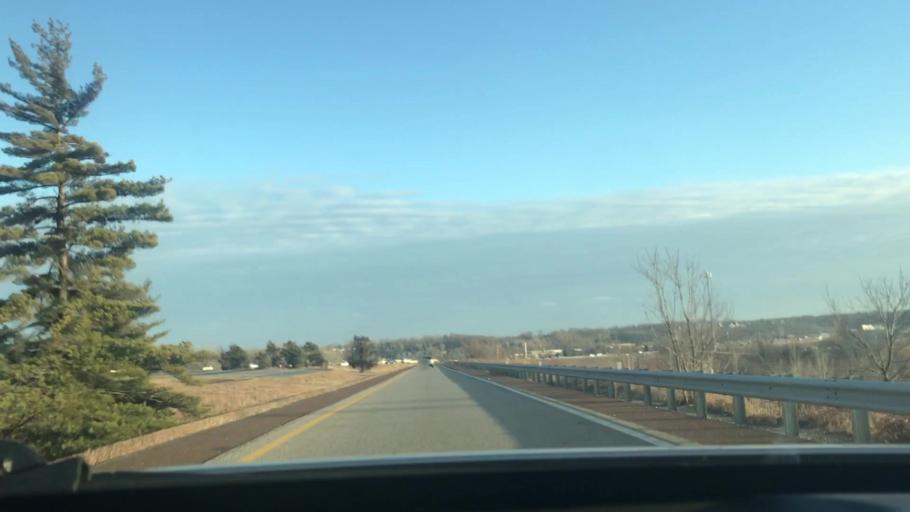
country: US
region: Missouri
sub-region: Jackson County
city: East Independence
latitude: 39.0405
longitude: -94.3655
